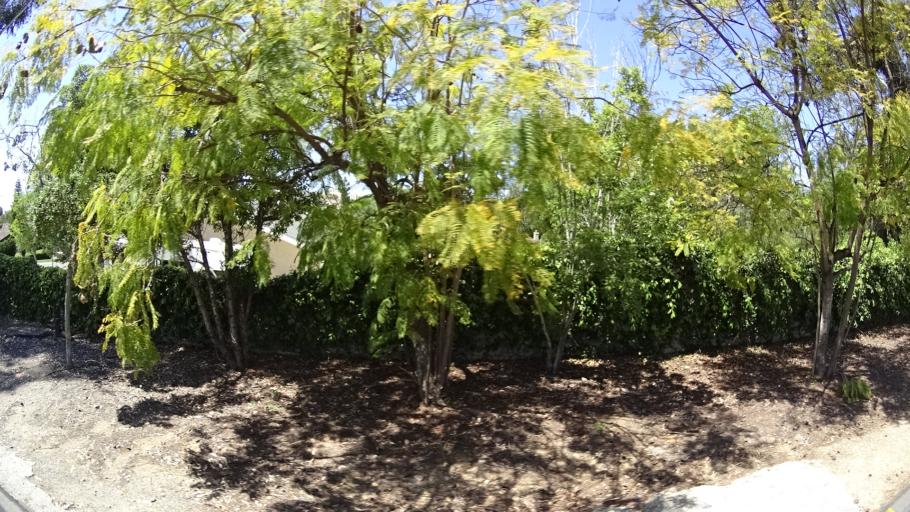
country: US
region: California
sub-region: Orange County
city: Villa Park
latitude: 33.8244
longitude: -117.7958
